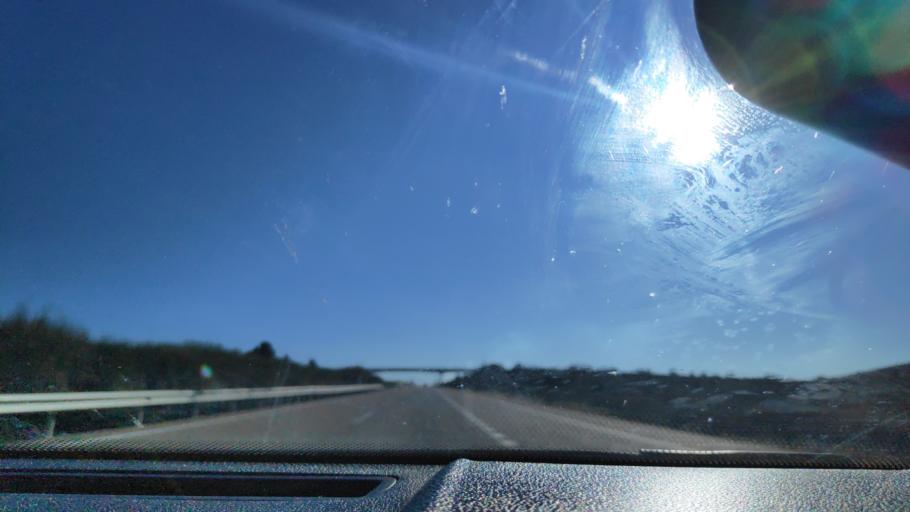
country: ES
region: Extremadura
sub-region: Provincia de Badajoz
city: Villafranca de los Barros
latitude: 38.5145
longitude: -6.3519
